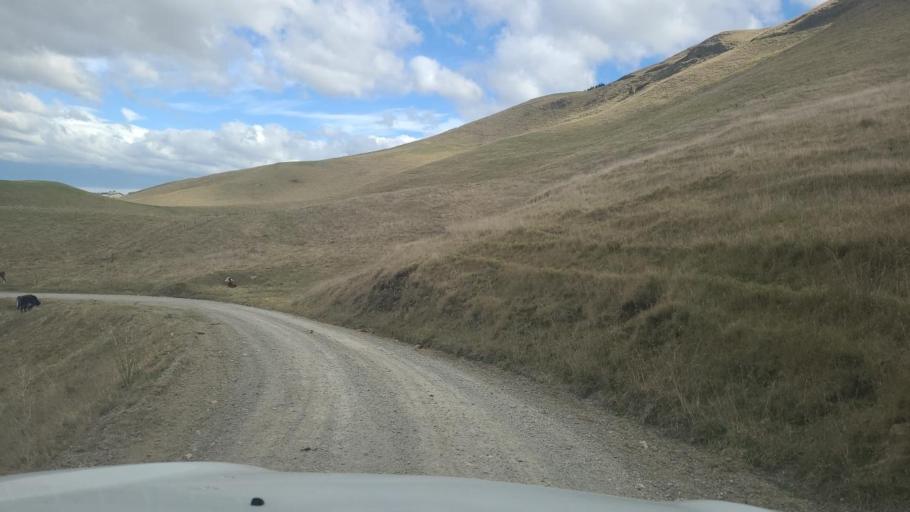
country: NZ
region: Hawke's Bay
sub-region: Hastings District
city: Hastings
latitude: -39.7545
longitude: 176.6879
